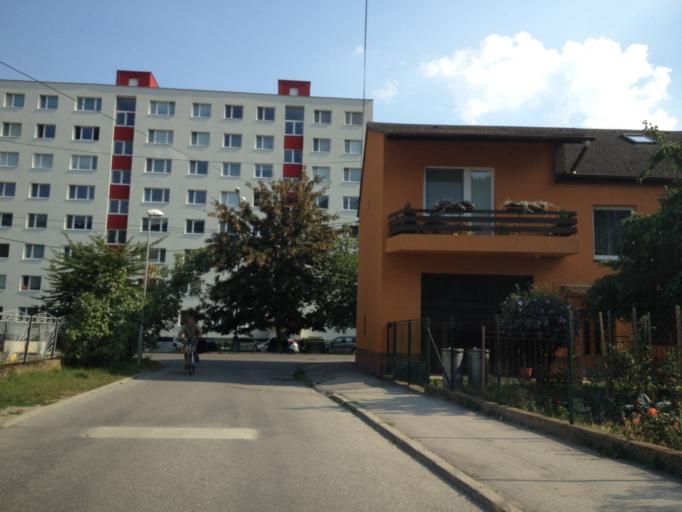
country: SK
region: Nitriansky
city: Puchov
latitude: 49.1263
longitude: 18.3231
